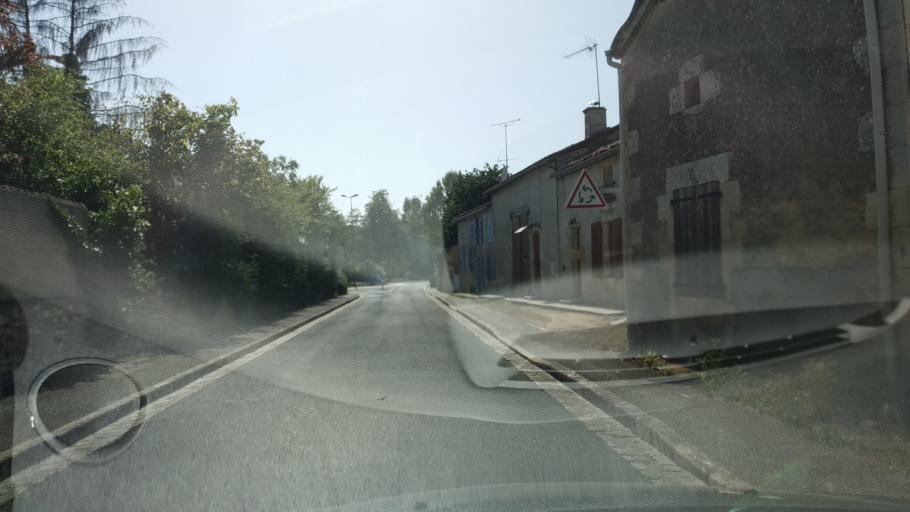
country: FR
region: Poitou-Charentes
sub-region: Departement de la Vienne
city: Lussac-les-Chateaux
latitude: 46.4449
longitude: 0.6630
